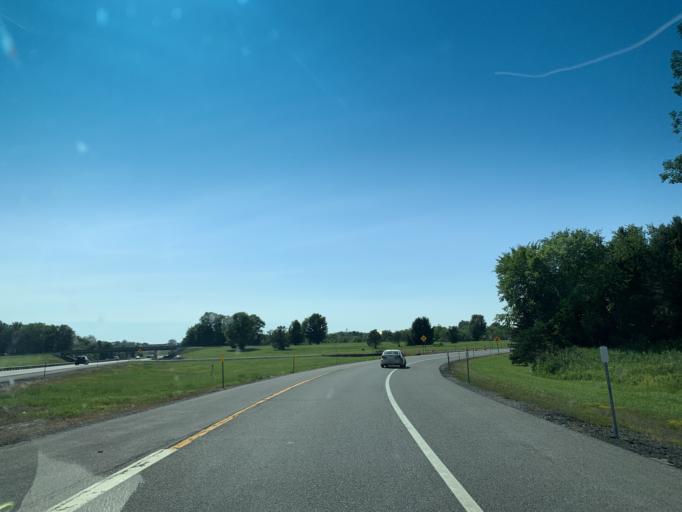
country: US
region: New York
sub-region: Oneida County
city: Sherrill
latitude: 43.1245
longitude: -75.5783
